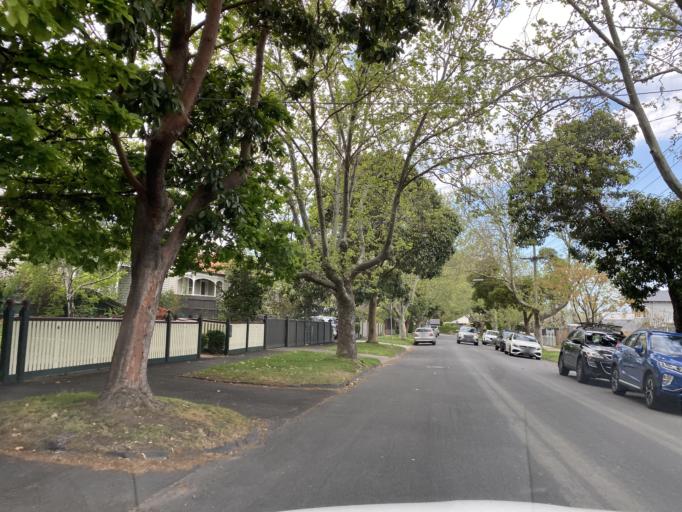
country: AU
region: Victoria
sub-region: Boroondara
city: Camberwell
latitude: -37.8310
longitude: 145.0742
